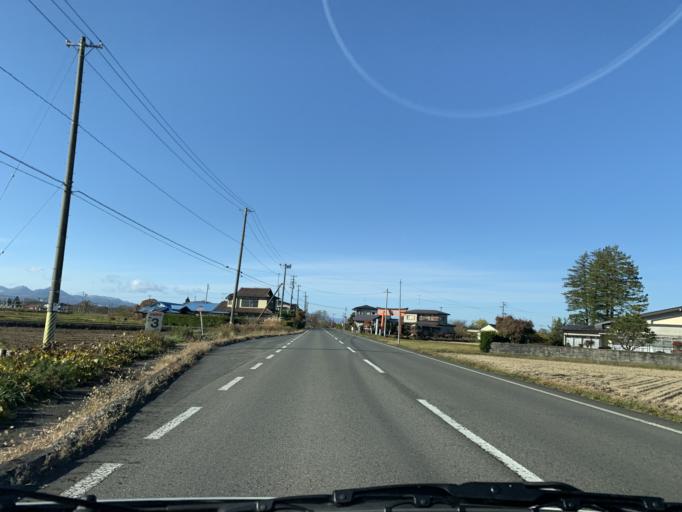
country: JP
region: Iwate
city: Mizusawa
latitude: 39.1809
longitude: 141.1321
